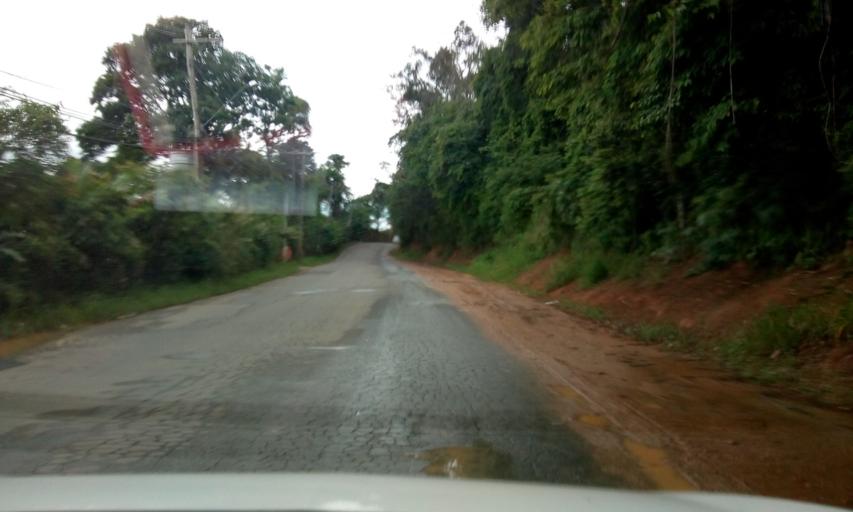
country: BR
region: Sao Paulo
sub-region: Itupeva
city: Itupeva
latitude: -23.1443
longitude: -47.0514
